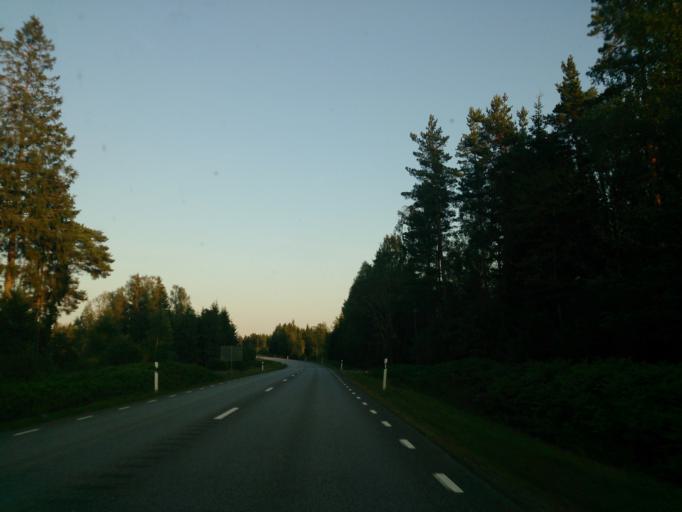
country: SE
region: Joenkoeping
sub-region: Varnamo Kommun
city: Rydaholm
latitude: 56.9638
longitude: 14.3397
